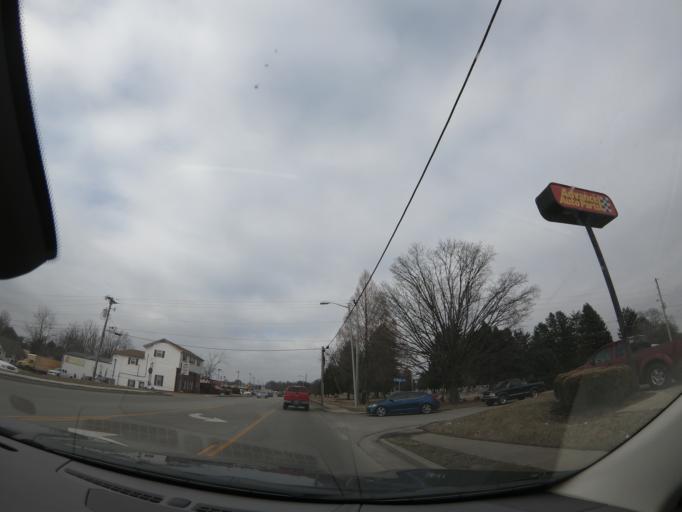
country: US
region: Kentucky
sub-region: Nelson County
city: Bardstown
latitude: 37.8219
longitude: -85.4626
